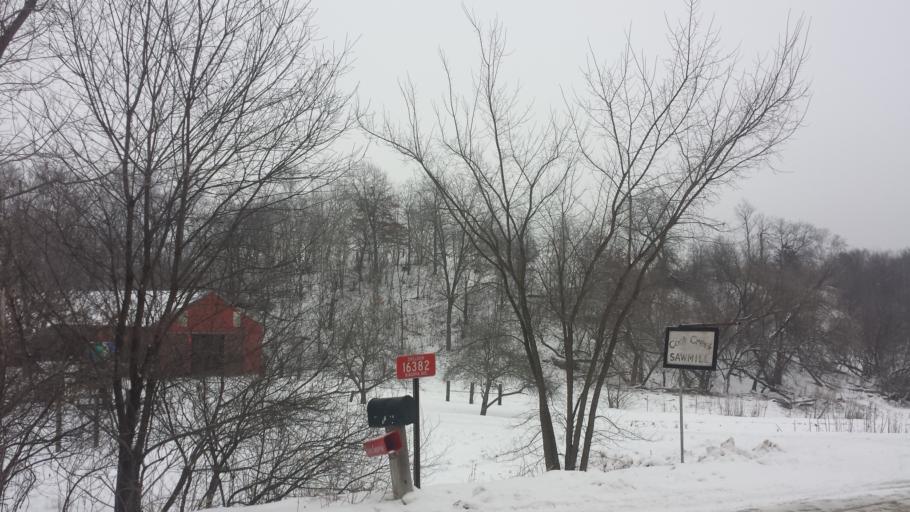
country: US
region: Wisconsin
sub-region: Monroe County
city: Cashton
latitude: 43.7781
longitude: -90.6593
